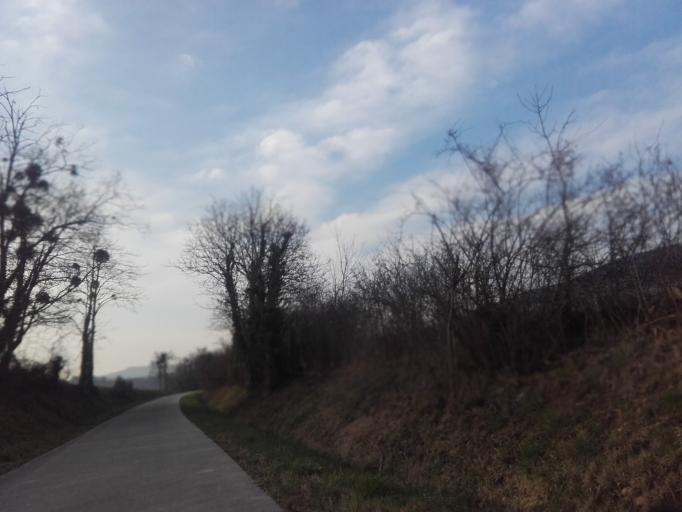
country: FR
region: Bourgogne
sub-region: Departement de la Cote-d'Or
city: Nolay
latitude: 46.9023
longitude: 4.6668
